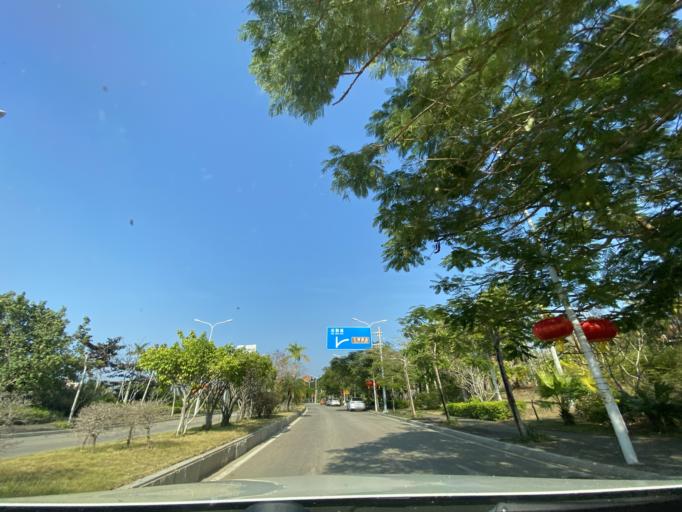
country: CN
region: Hainan
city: Haitangwan
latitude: 18.4036
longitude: 109.7785
